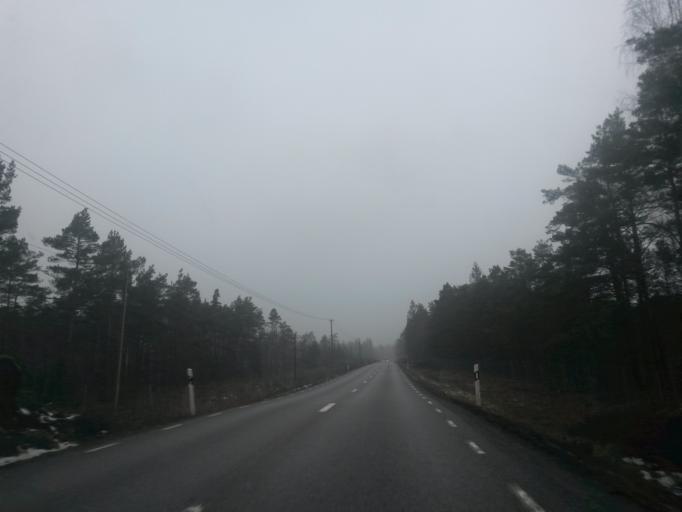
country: SE
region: Vaestra Goetaland
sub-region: Alingsas Kommun
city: Sollebrunn
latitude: 58.1946
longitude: 12.4314
